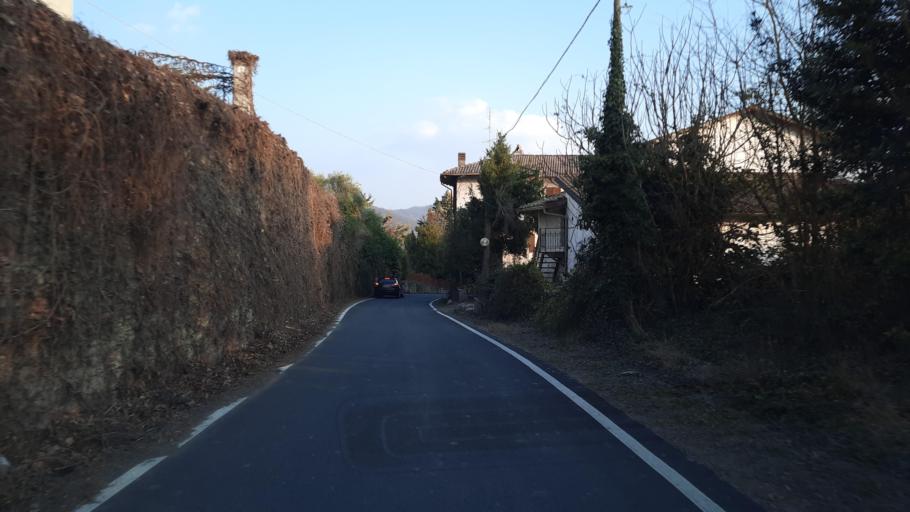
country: IT
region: Piedmont
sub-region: Provincia di Alessandria
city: Odalengo Grande
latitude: 45.1019
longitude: 8.1768
